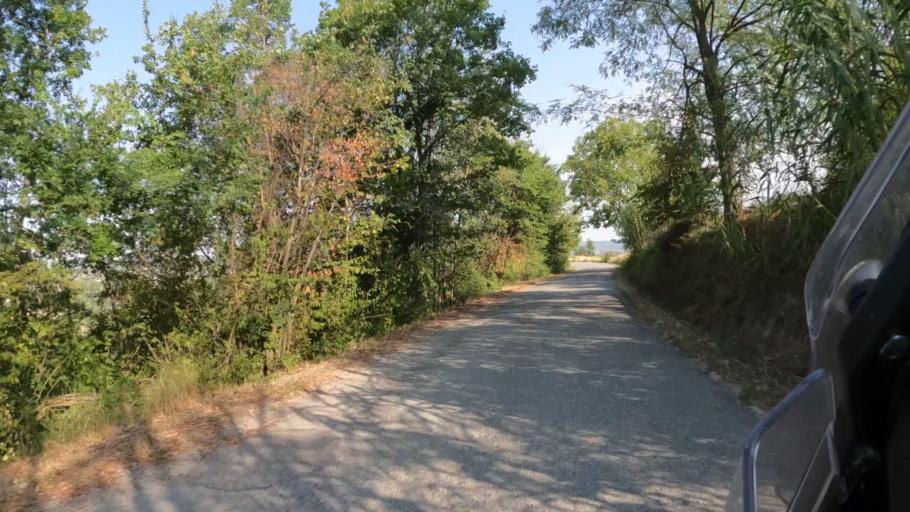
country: IT
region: Piedmont
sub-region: Provincia di Asti
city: Nizza Monferrato
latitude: 44.7593
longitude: 8.3801
